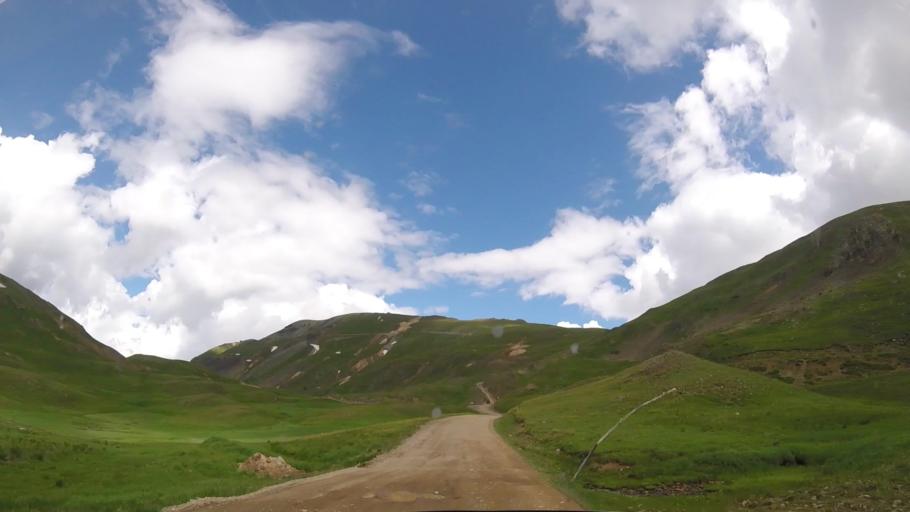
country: US
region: Colorado
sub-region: Ouray County
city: Ouray
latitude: 37.9553
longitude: -107.5750
